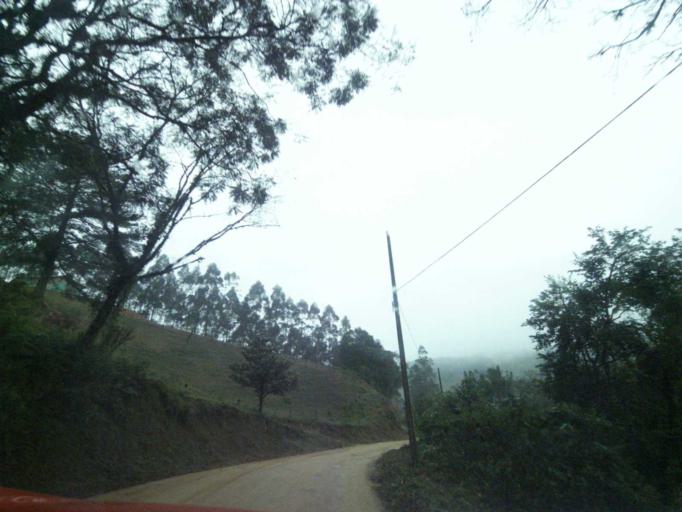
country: BR
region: Santa Catarina
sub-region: Anitapolis
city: Anitapolis
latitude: -27.9233
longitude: -49.1306
